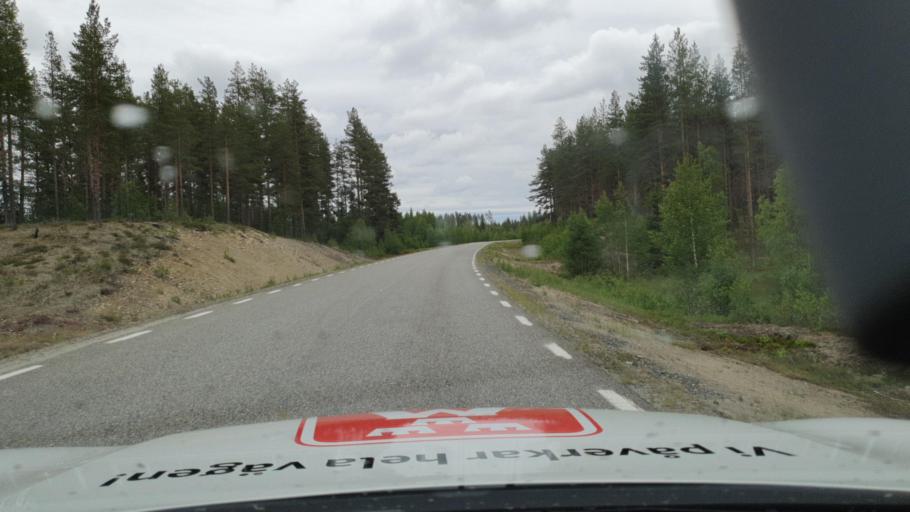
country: SE
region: Vaesterbotten
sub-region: Lycksele Kommun
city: Lycksele
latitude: 64.2159
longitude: 18.2629
